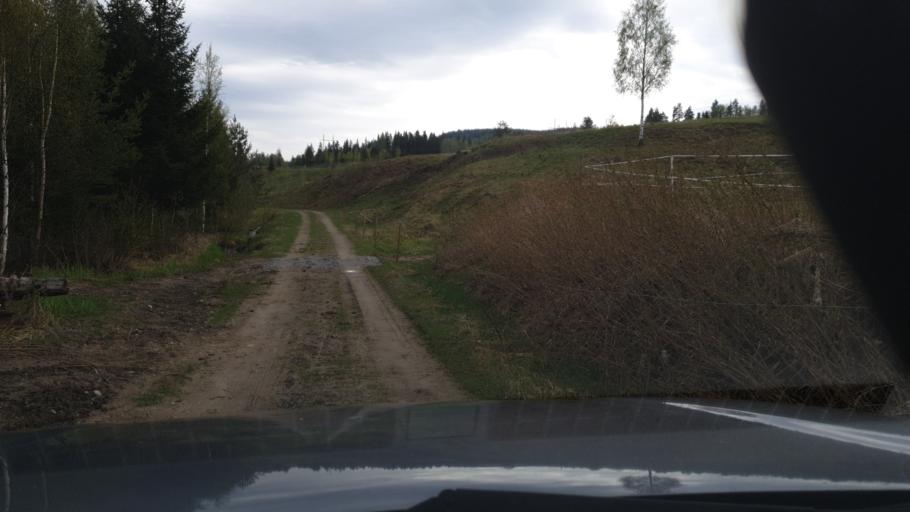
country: SE
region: Gaevleborg
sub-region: Ljusdals Kommun
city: Jaervsoe
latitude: 61.7373
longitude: 16.2809
